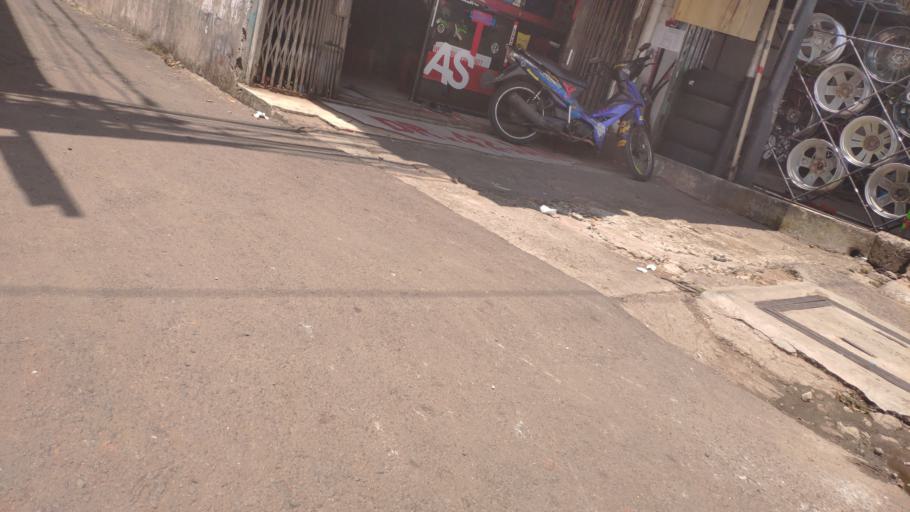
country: ID
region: Jakarta Raya
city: Jakarta
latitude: -6.2732
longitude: 106.8303
